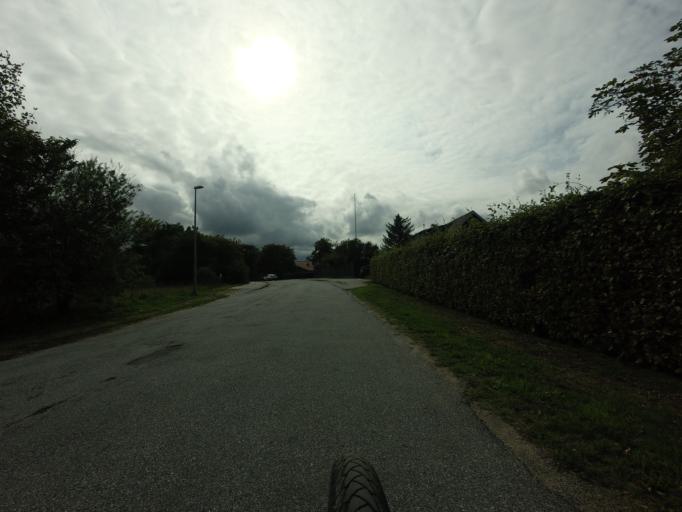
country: DK
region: North Denmark
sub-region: Hjorring Kommune
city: Hjorring
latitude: 57.4864
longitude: 9.9931
